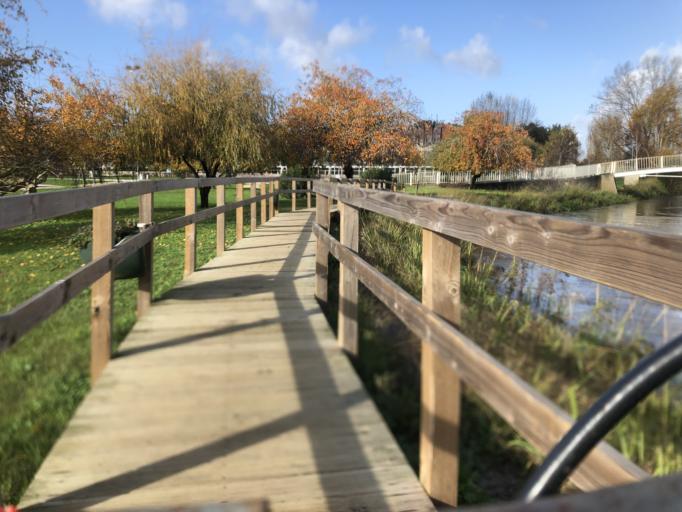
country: PT
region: Aveiro
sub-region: Estarreja
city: Estarreja
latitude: 40.7526
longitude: -8.5648
